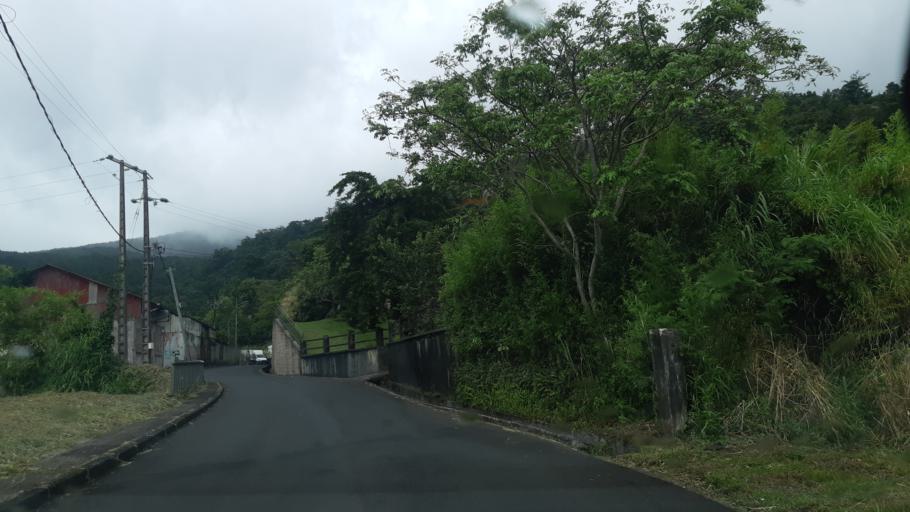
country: GP
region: Guadeloupe
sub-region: Guadeloupe
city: Saint-Claude
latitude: 16.0436
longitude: -61.6936
